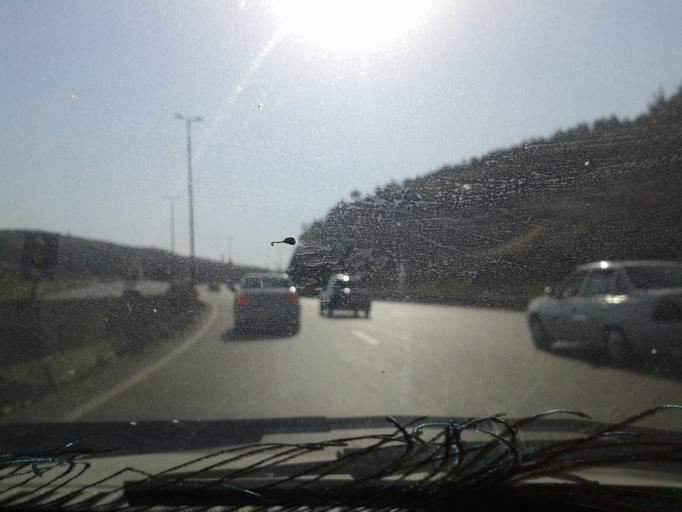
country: IR
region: Tehran
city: Tehran
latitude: 35.7358
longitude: 51.6737
